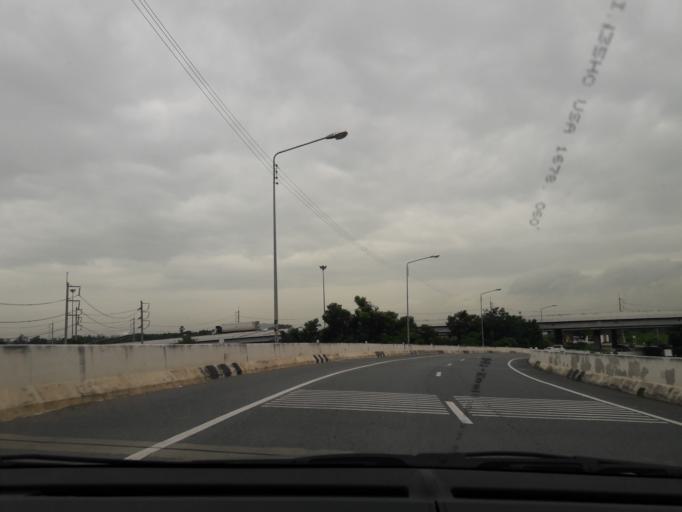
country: TH
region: Sara Buri
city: Saraburi
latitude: 14.5407
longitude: 100.9529
